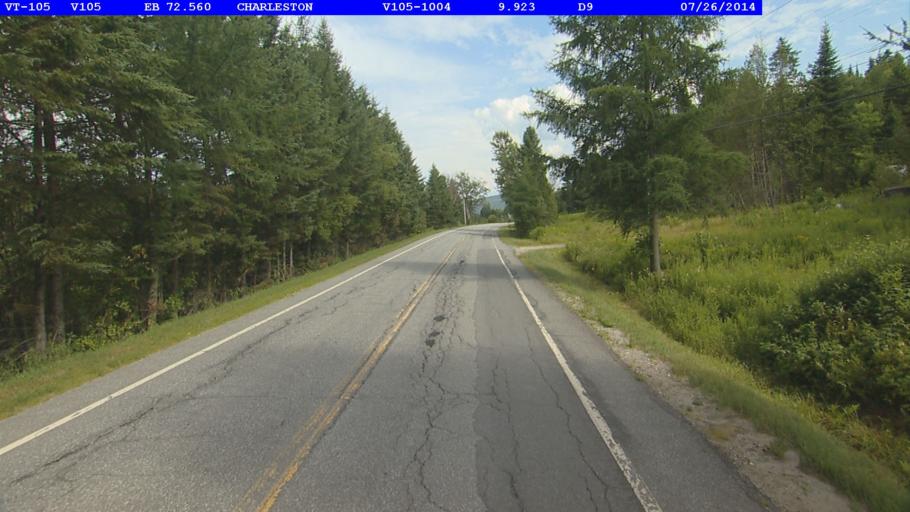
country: US
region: Vermont
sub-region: Orleans County
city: Newport
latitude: 44.8149
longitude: -71.9481
